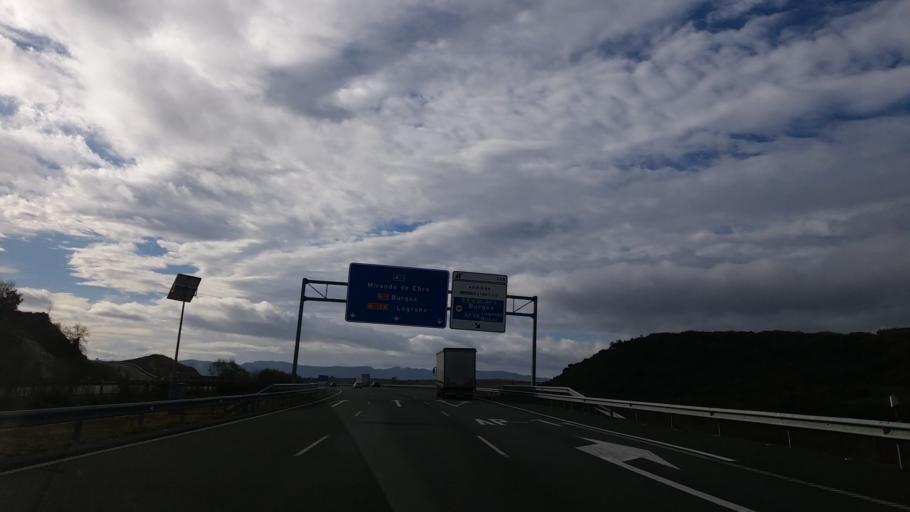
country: ES
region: Basque Country
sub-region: Provincia de Alava
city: Arminon
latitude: 42.7355
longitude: -2.8709
